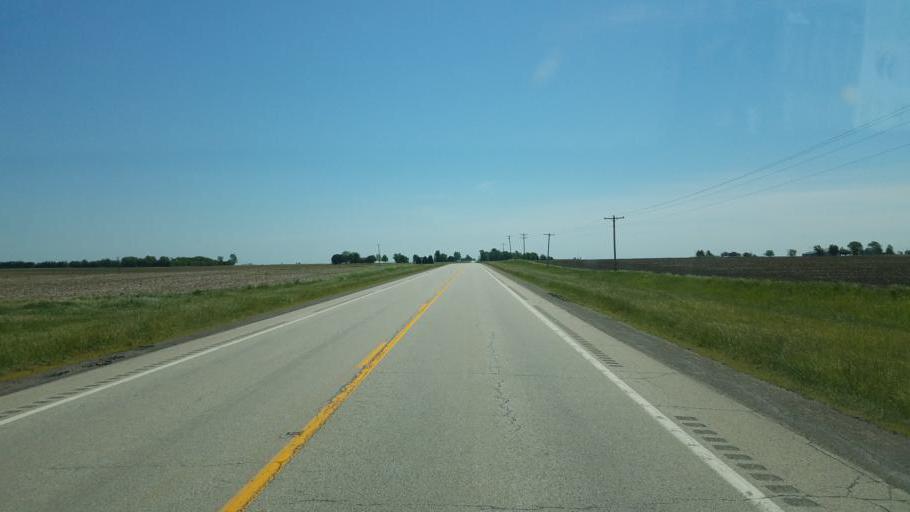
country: US
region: Illinois
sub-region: McLean County
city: Heyworth
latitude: 40.3123
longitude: -88.9285
